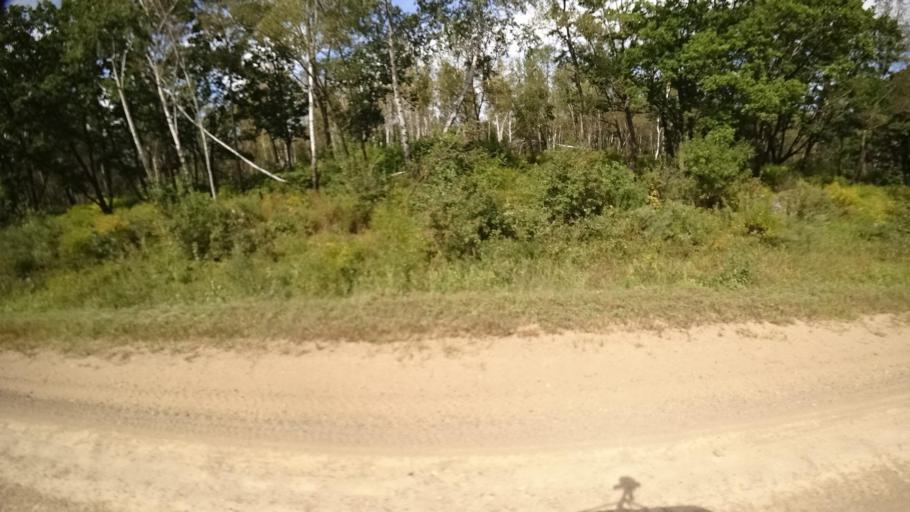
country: RU
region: Primorskiy
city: Yakovlevka
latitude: 44.6976
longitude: 133.6244
